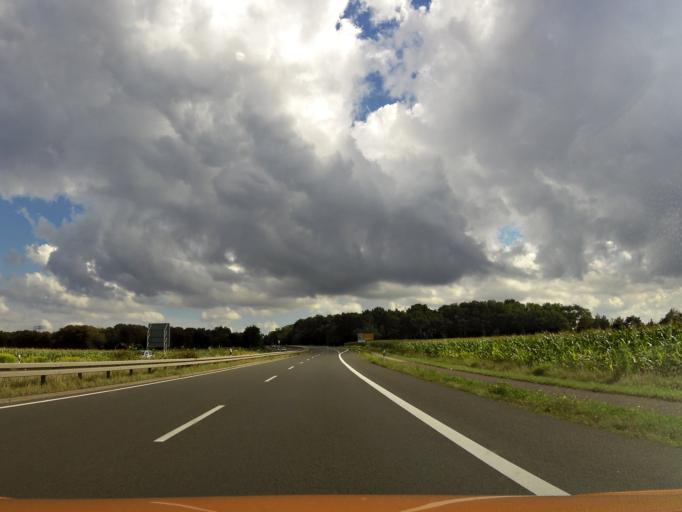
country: DE
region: Brandenburg
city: Wustermark
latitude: 52.4715
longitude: 12.9557
